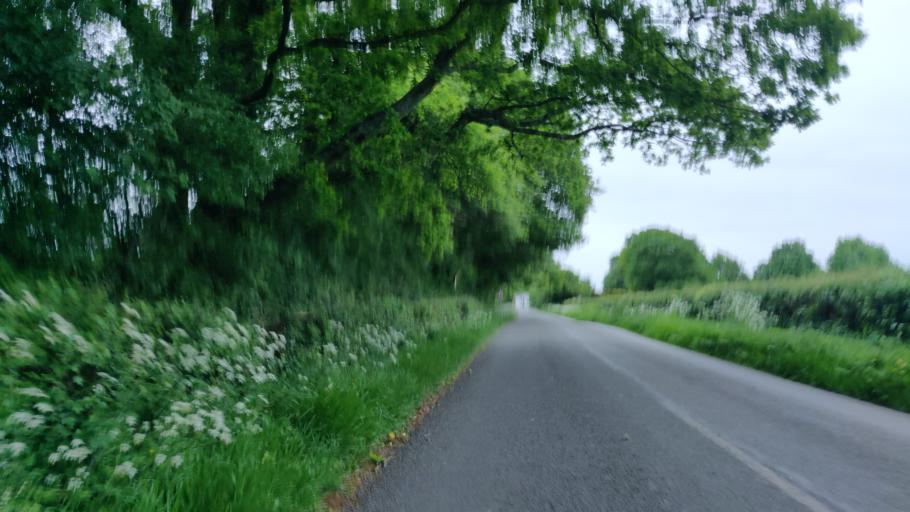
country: GB
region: England
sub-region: West Sussex
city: Southwater
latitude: 51.0309
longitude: -0.3663
